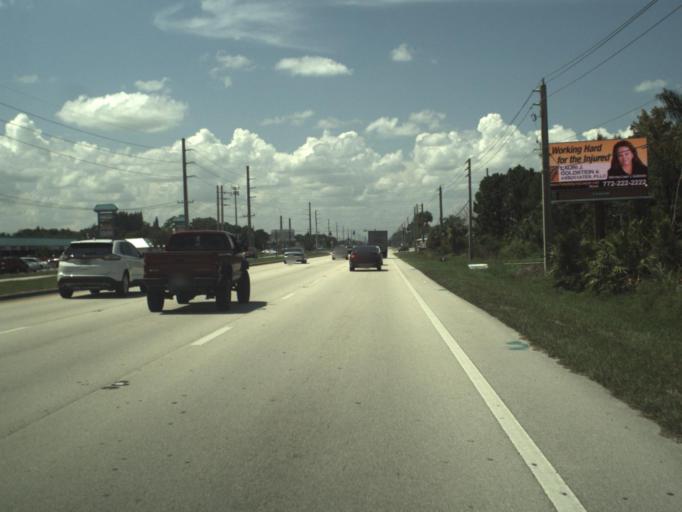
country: US
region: Florida
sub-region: Martin County
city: North River Shores
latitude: 27.2197
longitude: -80.2624
